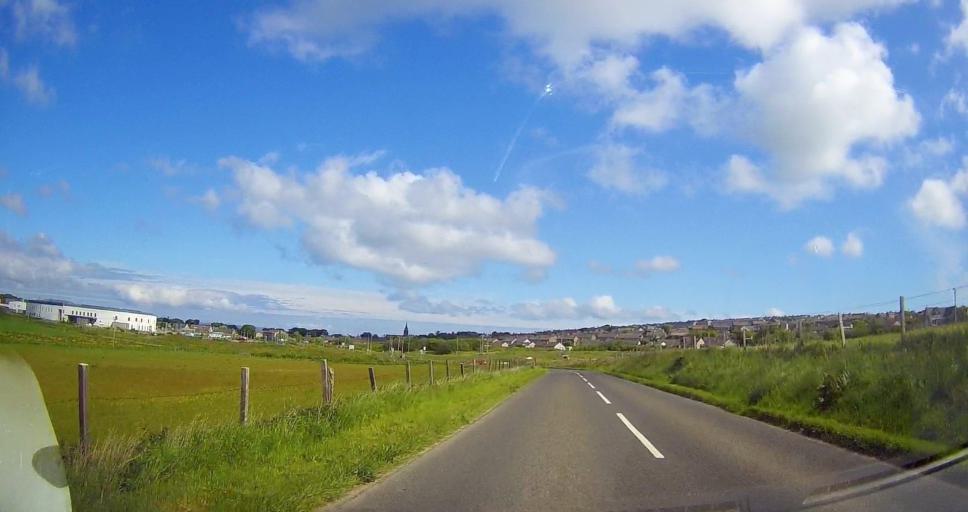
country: GB
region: Scotland
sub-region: Orkney Islands
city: Orkney
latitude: 58.9702
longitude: -2.9623
